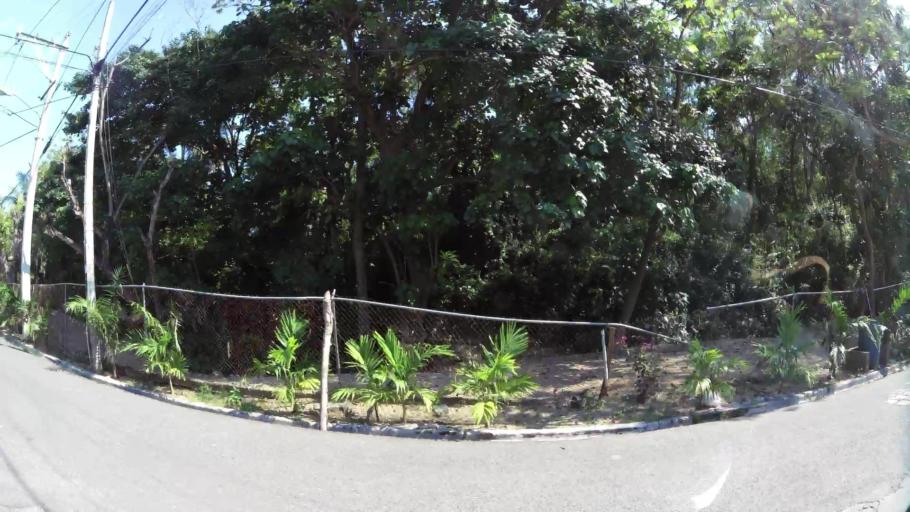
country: DO
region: Santo Domingo
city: Santo Domingo Oeste
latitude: 18.4742
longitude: -70.0019
